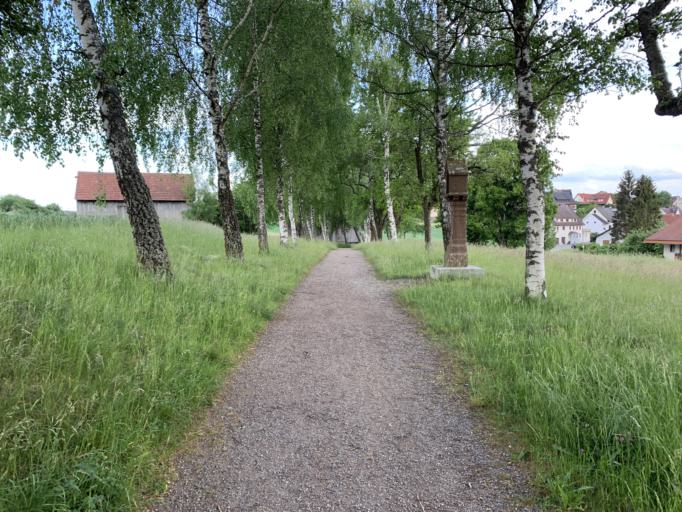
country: DE
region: Baden-Wuerttemberg
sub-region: Freiburg Region
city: Loffingen
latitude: 47.8906
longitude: 8.3412
